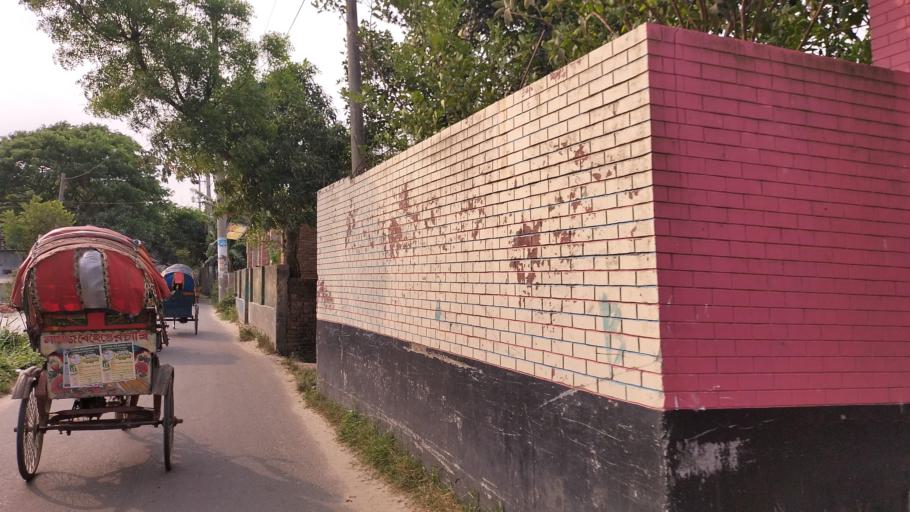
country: BD
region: Dhaka
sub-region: Dhaka
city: Dhaka
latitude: 23.6658
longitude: 90.3508
